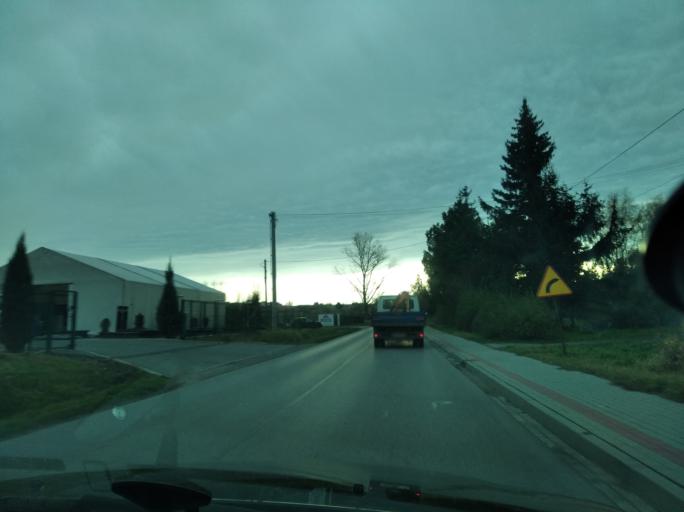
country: PL
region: Subcarpathian Voivodeship
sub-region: Powiat rzeszowski
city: Niechobrz
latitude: 50.0200
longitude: 21.8816
